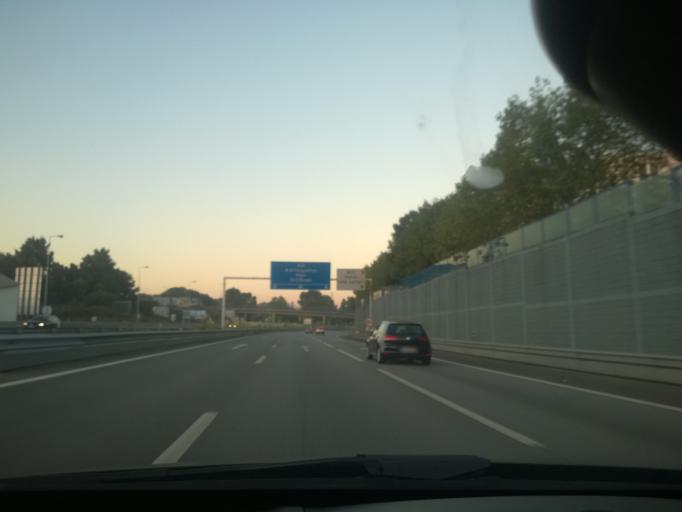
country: PT
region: Porto
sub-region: Maia
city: Gemunde
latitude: 41.2392
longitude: -8.6504
